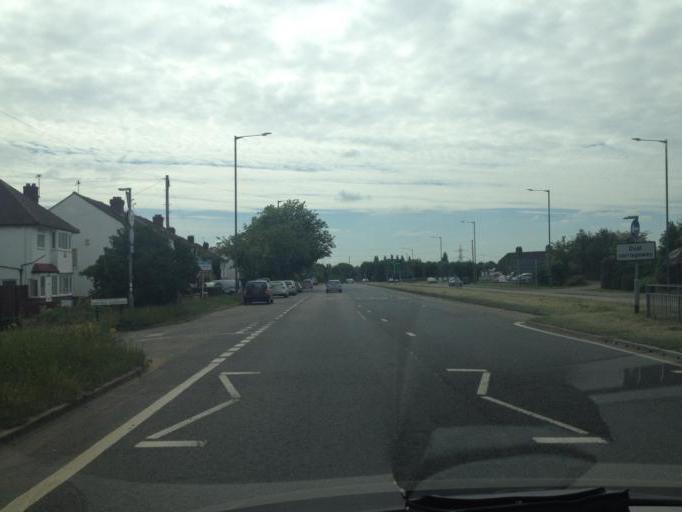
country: GB
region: England
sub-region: Buckinghamshire
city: Denham
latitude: 51.5657
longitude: -0.5004
